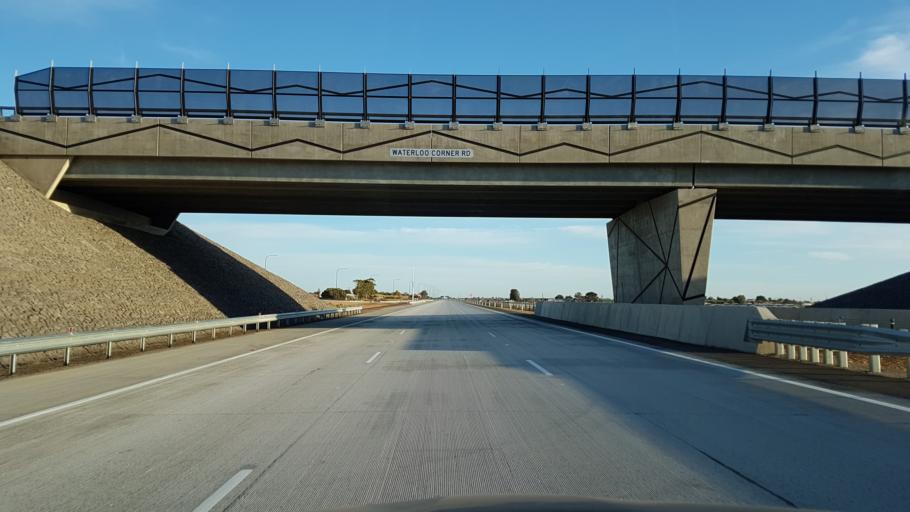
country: AU
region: South Australia
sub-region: Salisbury
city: Salisbury
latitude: -34.7332
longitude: 138.5767
